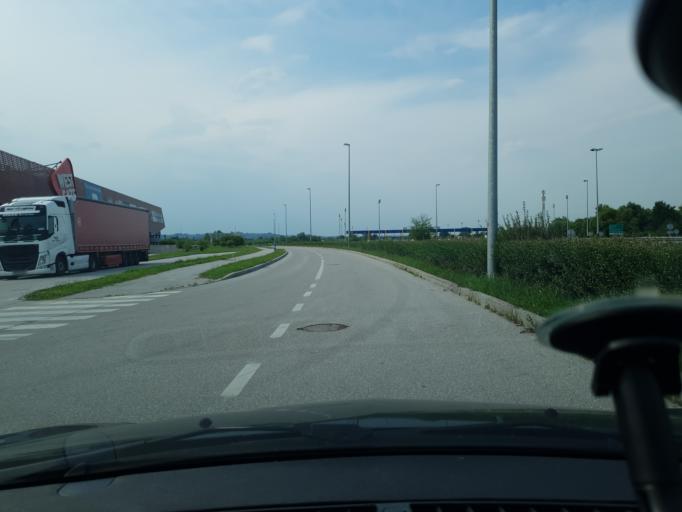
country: HR
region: Zagrebacka
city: Jablanovec
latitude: 45.8711
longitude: 15.8303
